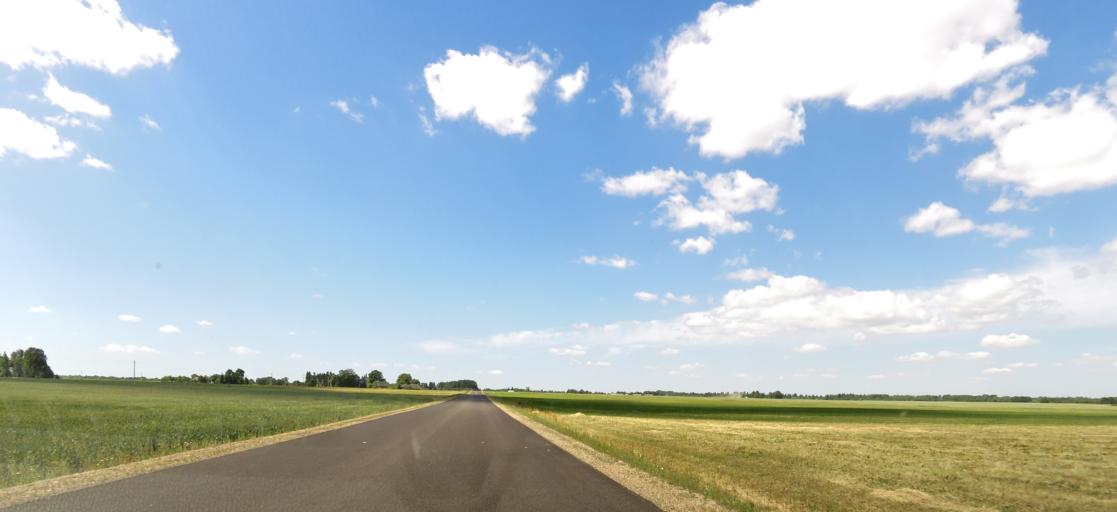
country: LT
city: Kupiskis
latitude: 55.9348
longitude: 24.9196
